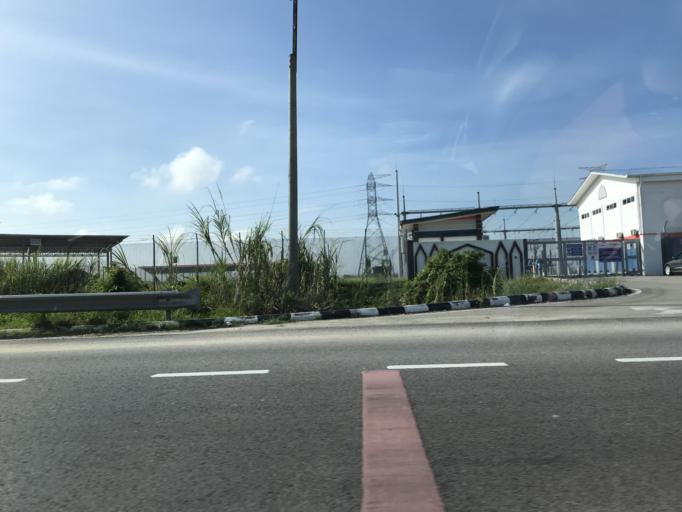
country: MY
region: Kelantan
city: Kampong Kadok
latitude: 6.0521
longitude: 102.2245
